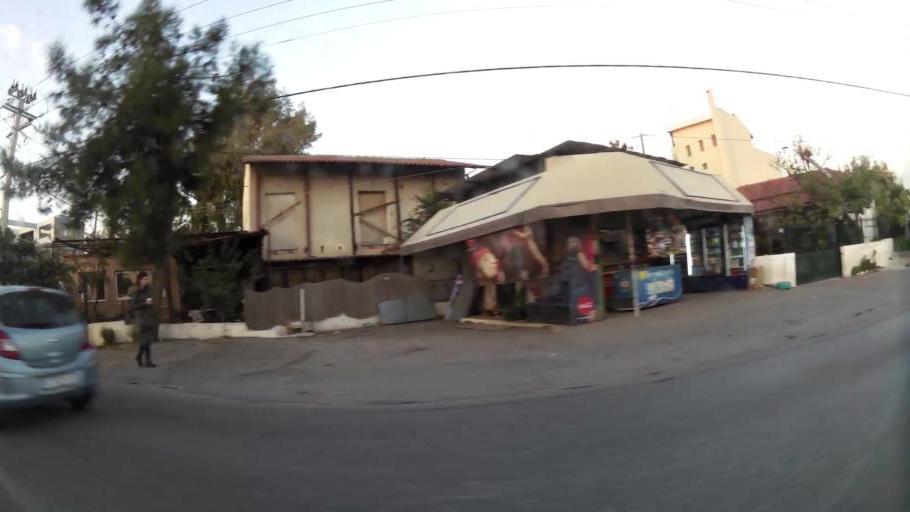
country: GR
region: Attica
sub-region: Nomarchia Anatolikis Attikis
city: Acharnes
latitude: 38.0943
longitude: 23.7523
